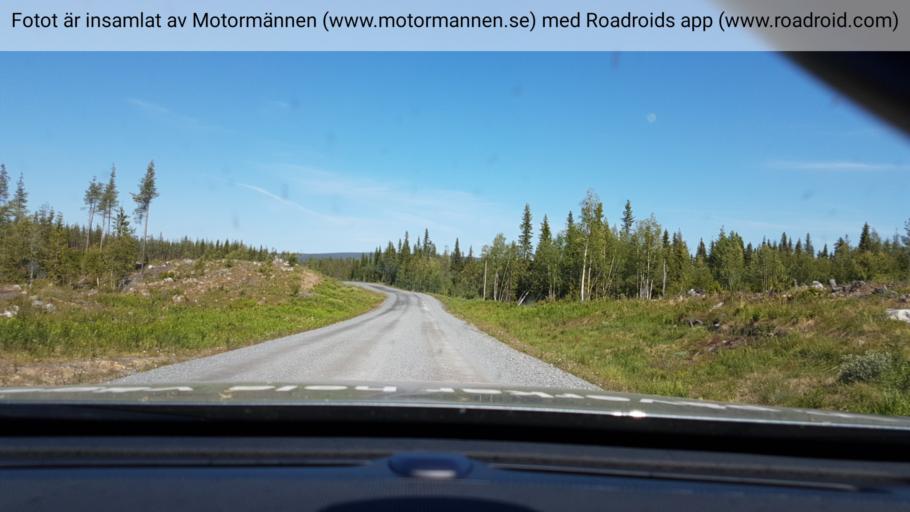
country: SE
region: Vaesterbotten
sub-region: Vilhelmina Kommun
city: Sjoberg
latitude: 64.6911
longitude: 15.7562
